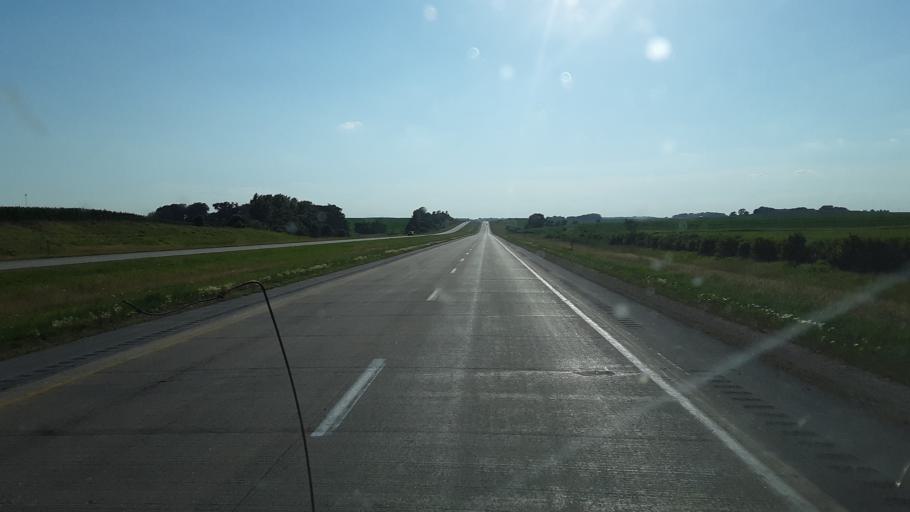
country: US
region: Iowa
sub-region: Hardin County
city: Iowa Falls
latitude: 42.4483
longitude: -93.3027
